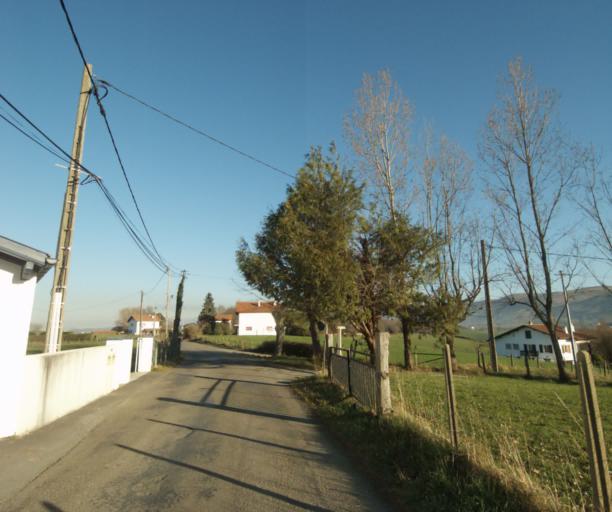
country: FR
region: Aquitaine
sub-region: Departement des Pyrenees-Atlantiques
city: Urrugne
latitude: 43.3503
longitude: -1.7094
